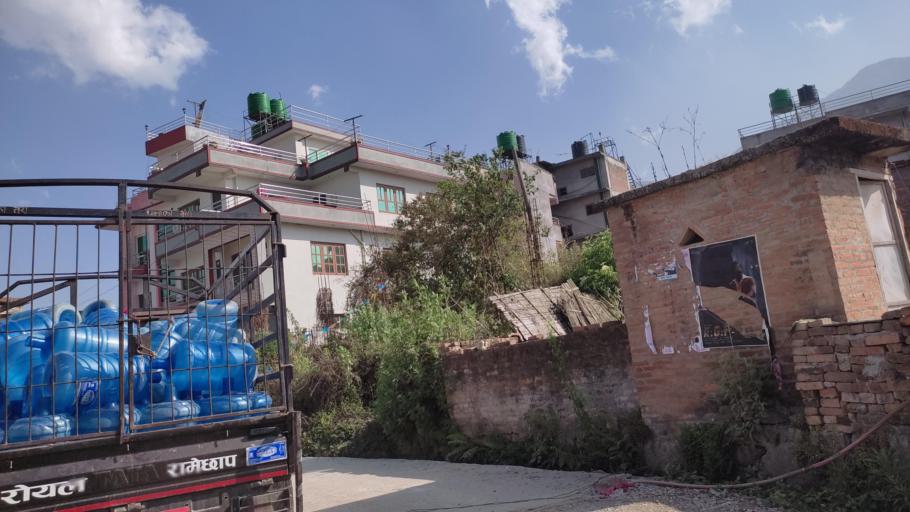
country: NP
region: Central Region
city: Kirtipur
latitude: 27.6762
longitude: 85.2535
